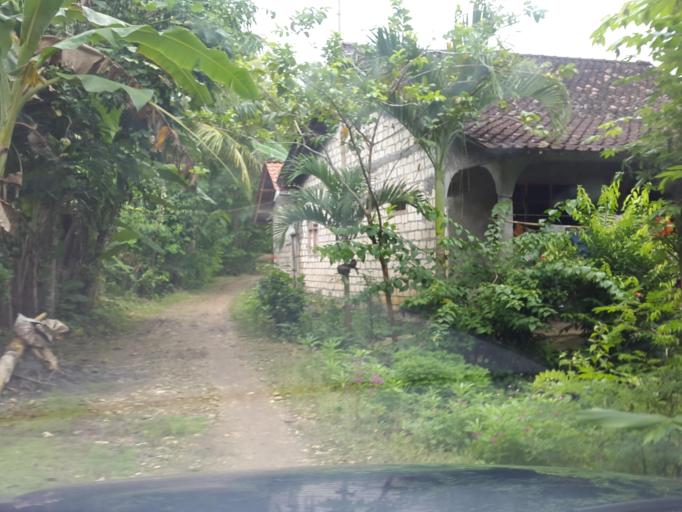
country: ID
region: Daerah Istimewa Yogyakarta
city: Wonosari
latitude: -7.9254
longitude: 110.6737
